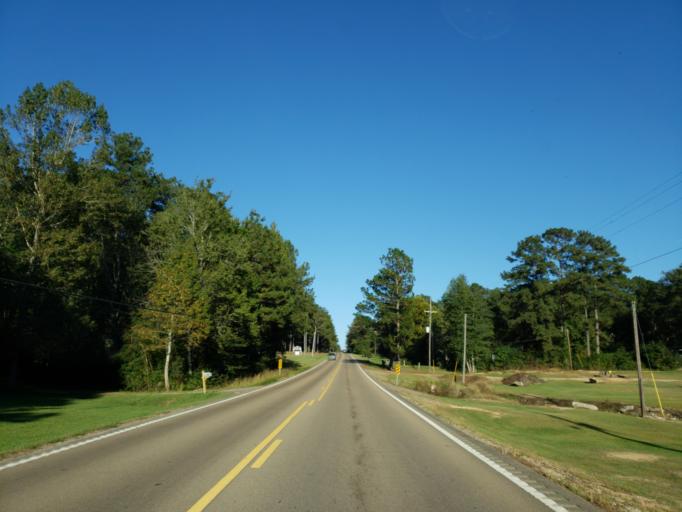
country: US
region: Mississippi
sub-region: Perry County
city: Richton
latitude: 31.3575
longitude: -88.9086
